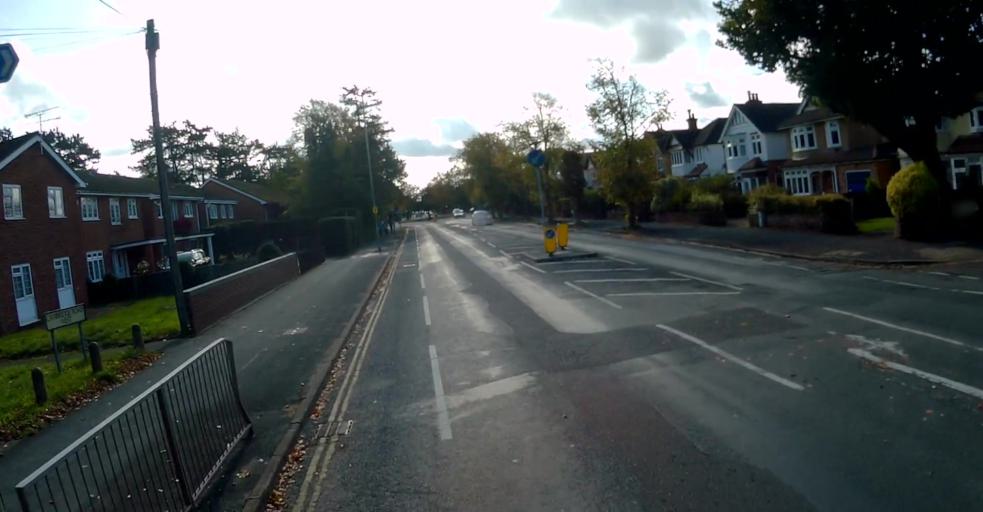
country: GB
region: England
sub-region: Hampshire
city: Farnborough
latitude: 51.2813
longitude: -0.7504
